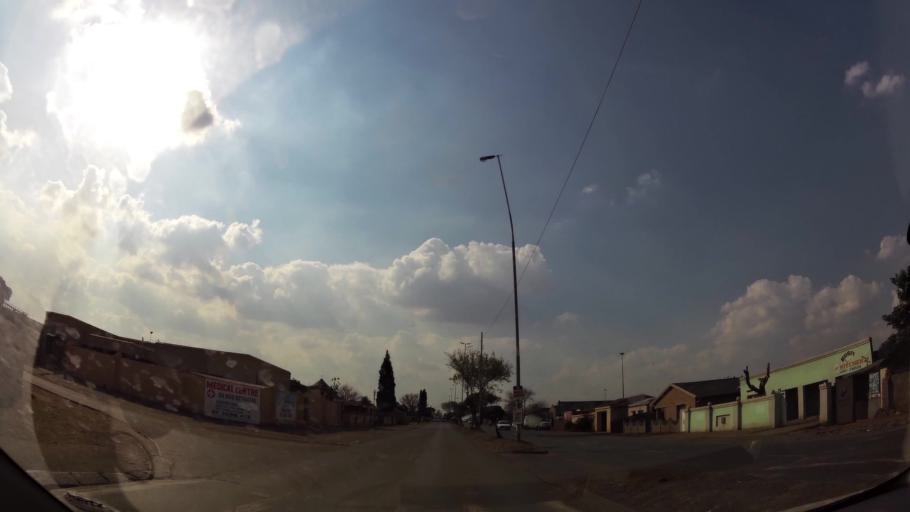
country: ZA
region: Gauteng
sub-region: Ekurhuleni Metropolitan Municipality
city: Germiston
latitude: -26.3212
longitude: 28.1491
